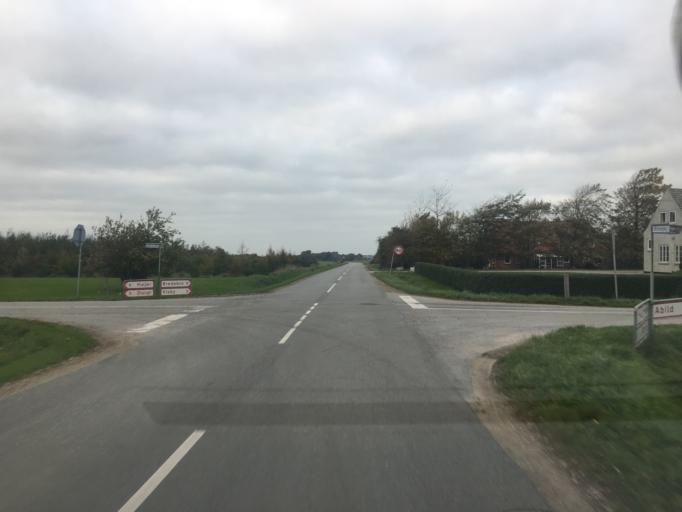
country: DE
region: Schleswig-Holstein
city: Aventoft
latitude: 54.9873
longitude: 8.7676
